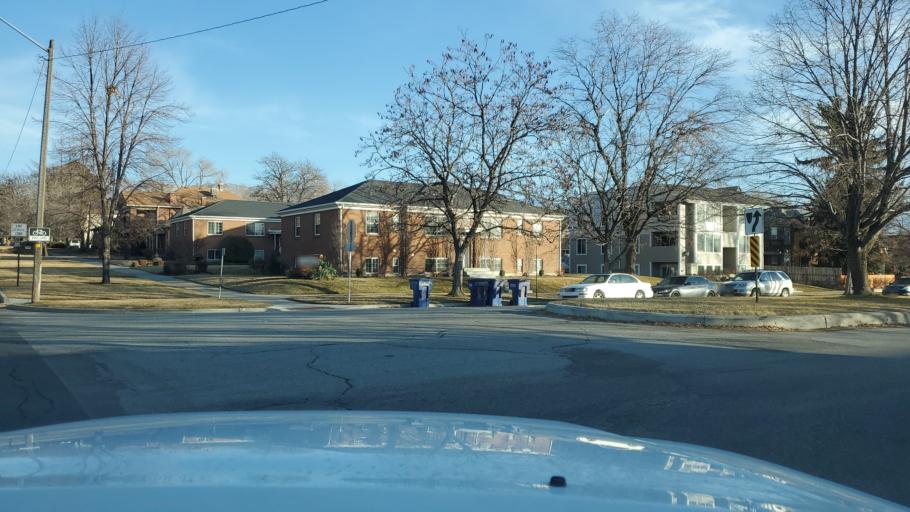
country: US
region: Utah
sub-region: Salt Lake County
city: Salt Lake City
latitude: 40.7628
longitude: -111.8683
